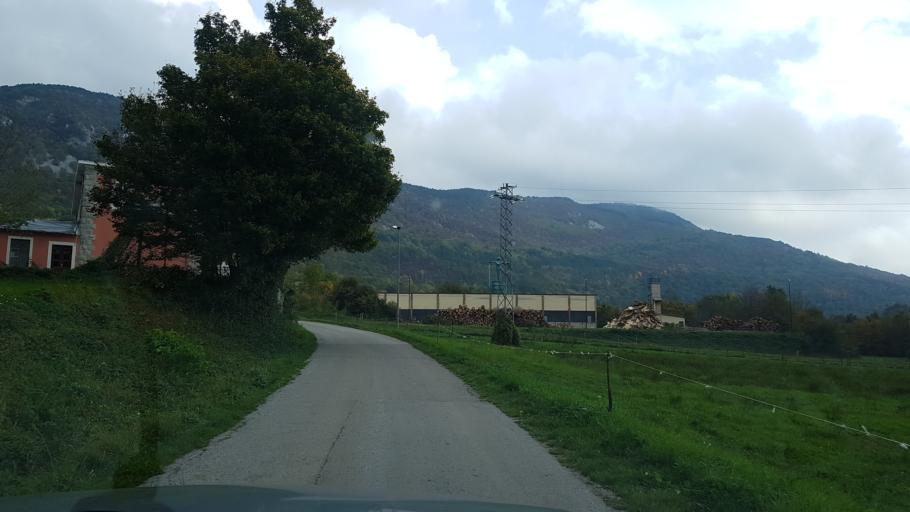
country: HR
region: Istarska
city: Buzet
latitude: 45.4078
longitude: 14.1126
